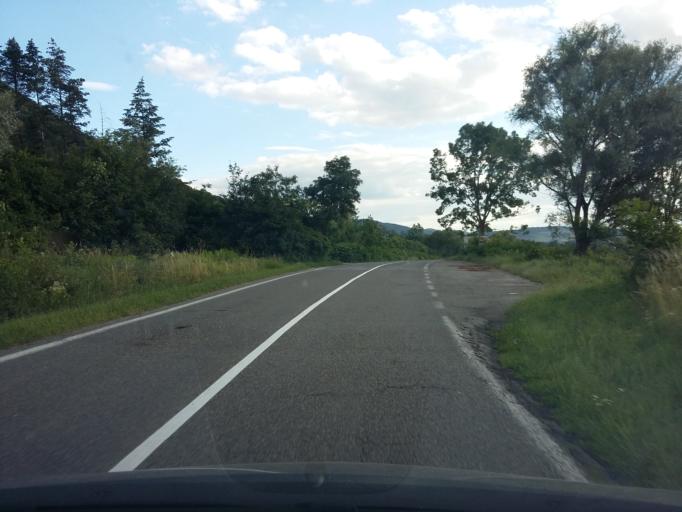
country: SK
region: Trnavsky
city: Smolenice
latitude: 48.5009
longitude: 17.2667
